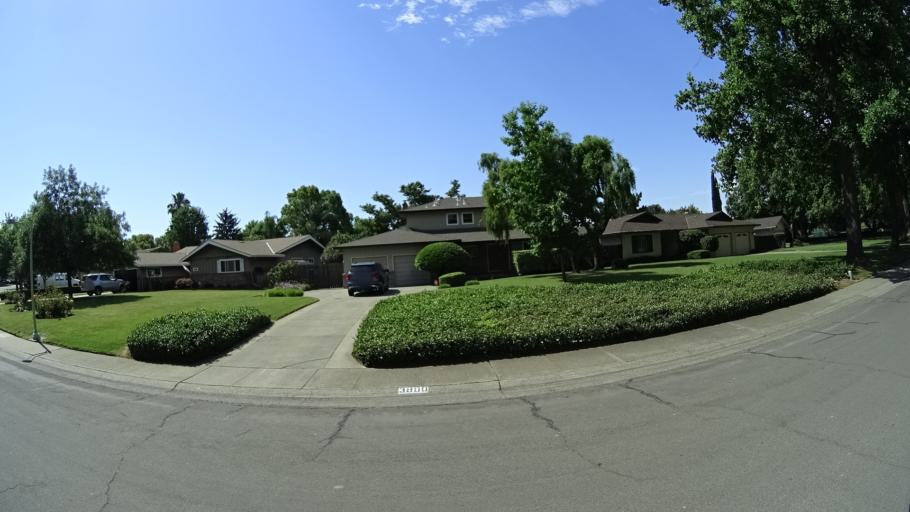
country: US
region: California
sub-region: Sacramento County
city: Sacramento
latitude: 38.5851
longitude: -121.4476
